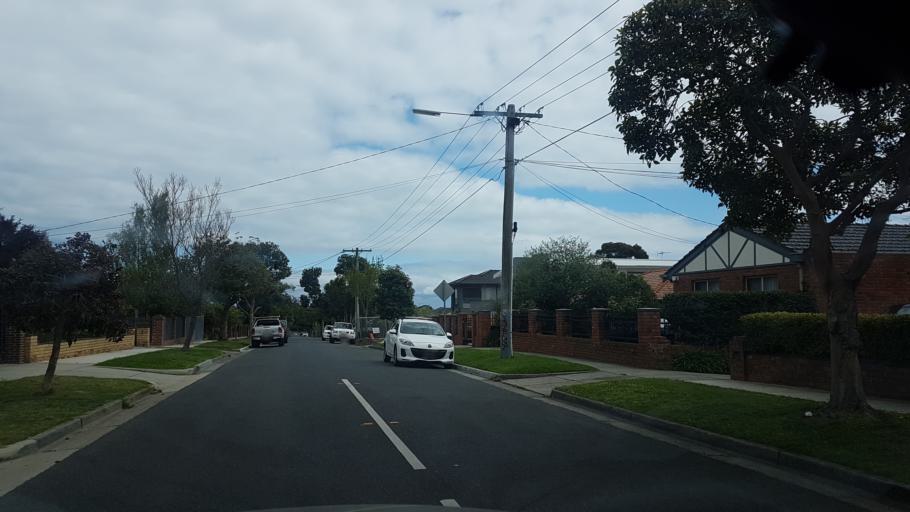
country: AU
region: Victoria
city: McKinnon
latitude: -37.9277
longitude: 145.0446
